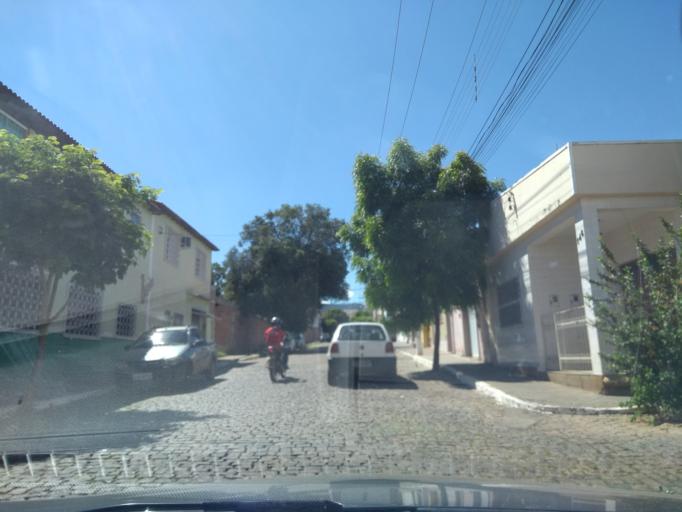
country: BR
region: Bahia
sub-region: Brumado
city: Brumado
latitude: -14.2066
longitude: -41.6671
